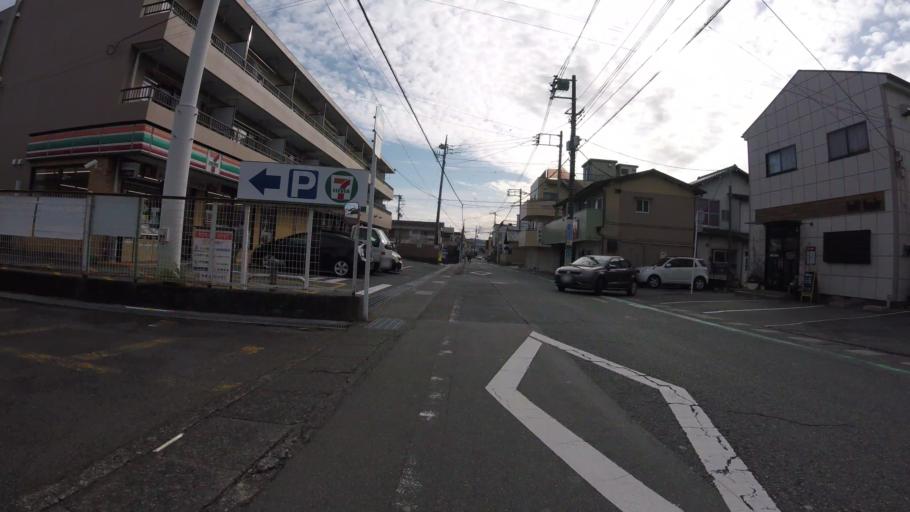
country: JP
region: Shizuoka
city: Mishima
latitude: 35.1152
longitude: 138.9176
